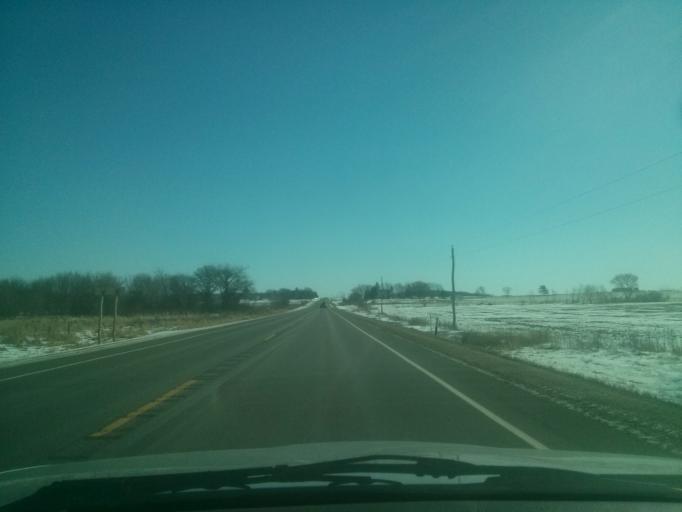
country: US
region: Wisconsin
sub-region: Polk County
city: Clear Lake
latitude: 45.1364
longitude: -92.3303
